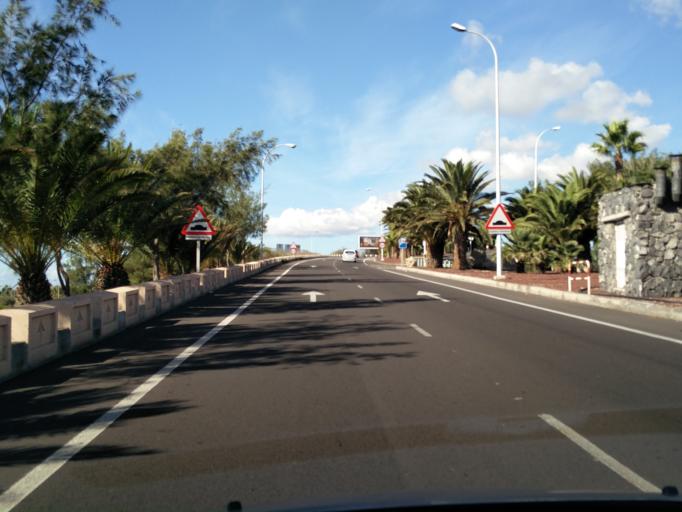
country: ES
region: Canary Islands
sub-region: Provincia de Santa Cruz de Tenerife
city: San Isidro
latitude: 28.0505
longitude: -16.5758
